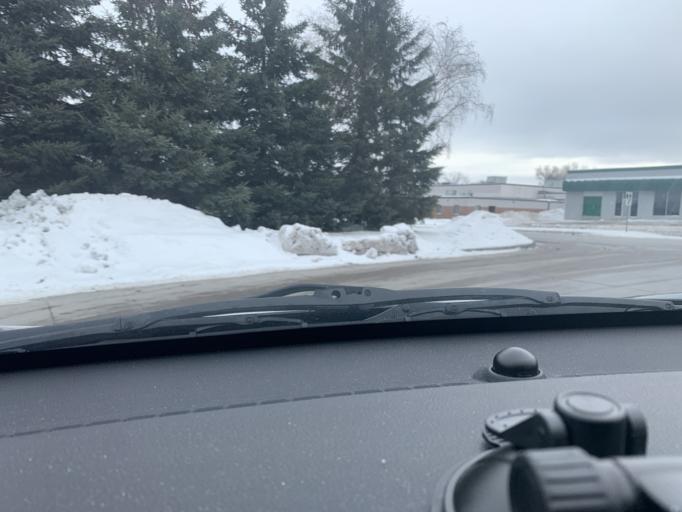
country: US
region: Minnesota
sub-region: Dakota County
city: West Saint Paul
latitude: 44.8924
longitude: -93.0770
